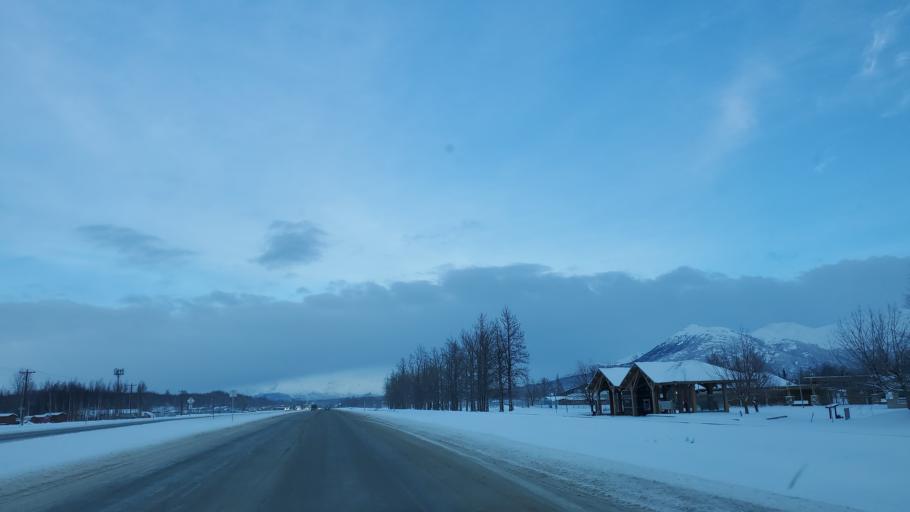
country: US
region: Alaska
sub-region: Matanuska-Susitna Borough
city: Palmer
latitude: 61.5781
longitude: -149.1399
